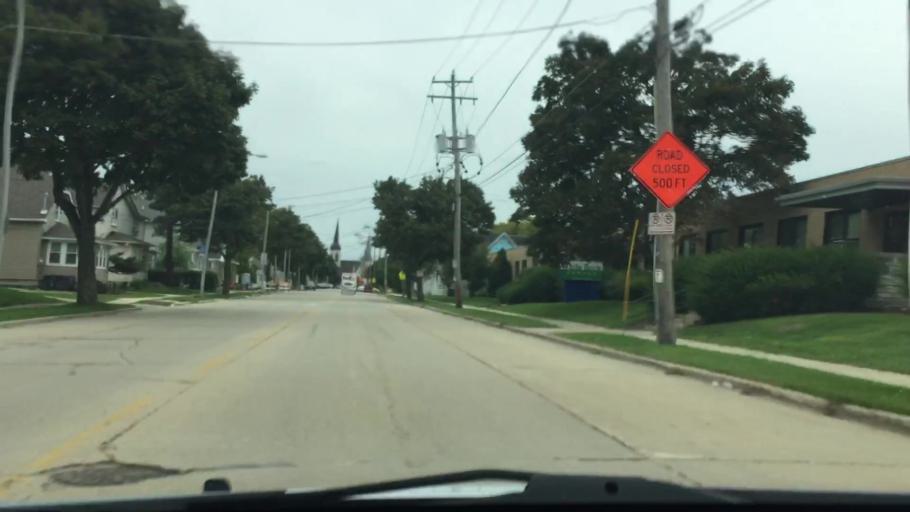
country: US
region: Wisconsin
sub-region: Waukesha County
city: Waukesha
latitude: 43.0170
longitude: -88.2227
